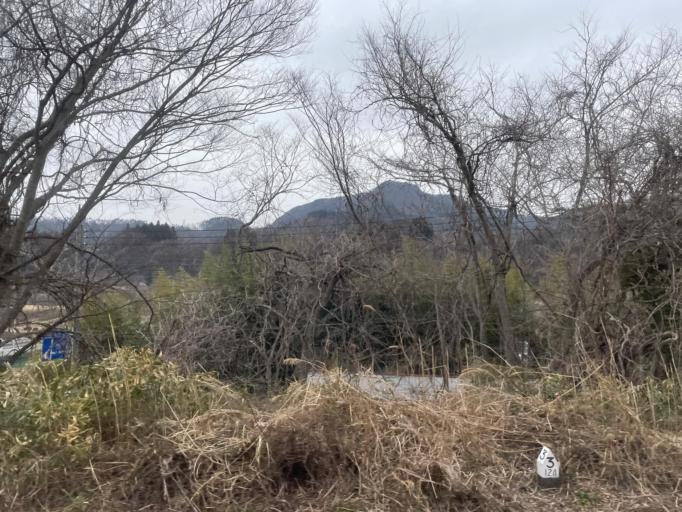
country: JP
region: Gunma
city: Numata
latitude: 36.7000
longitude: 138.9832
